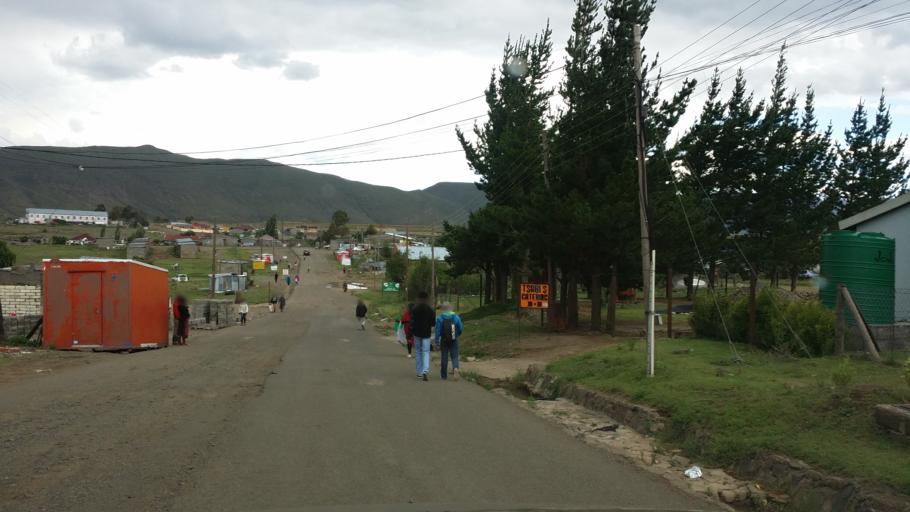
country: LS
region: Mokhotlong
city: Mokhotlong
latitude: -29.2869
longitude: 29.0658
